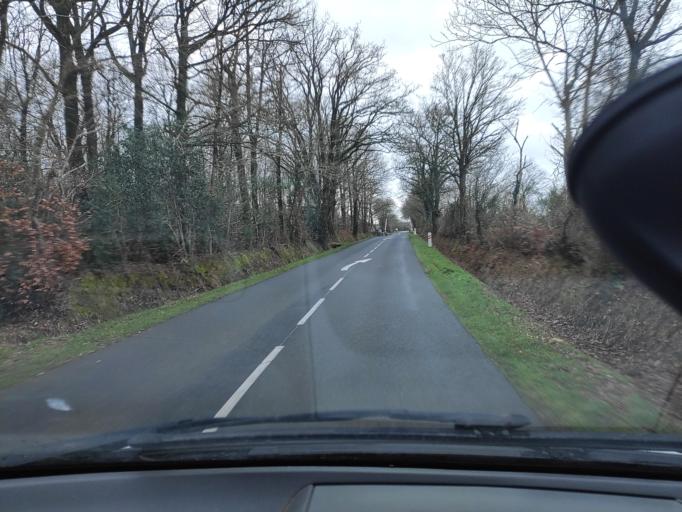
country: FR
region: Pays de la Loire
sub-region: Departement de la Vendee
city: La Ferriere
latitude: 46.6836
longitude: -1.3479
